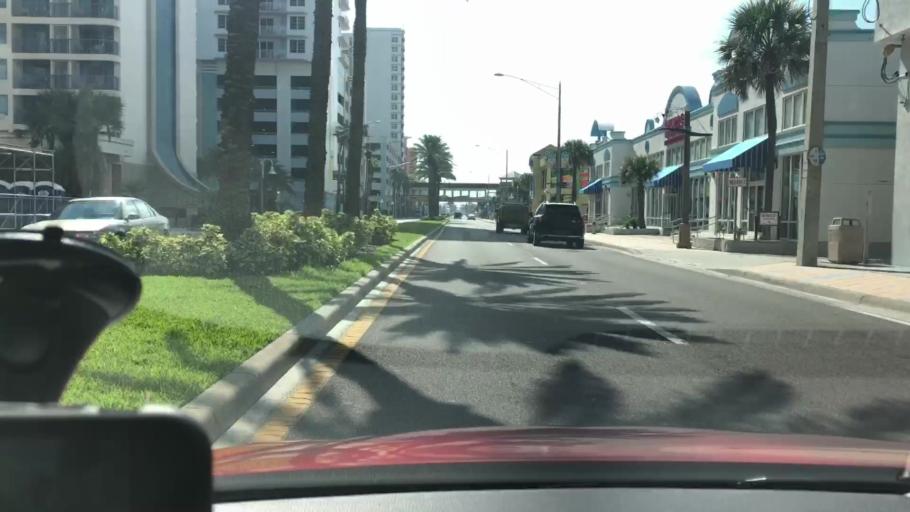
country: US
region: Florida
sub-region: Volusia County
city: Daytona Beach
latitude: 29.2335
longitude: -81.0115
